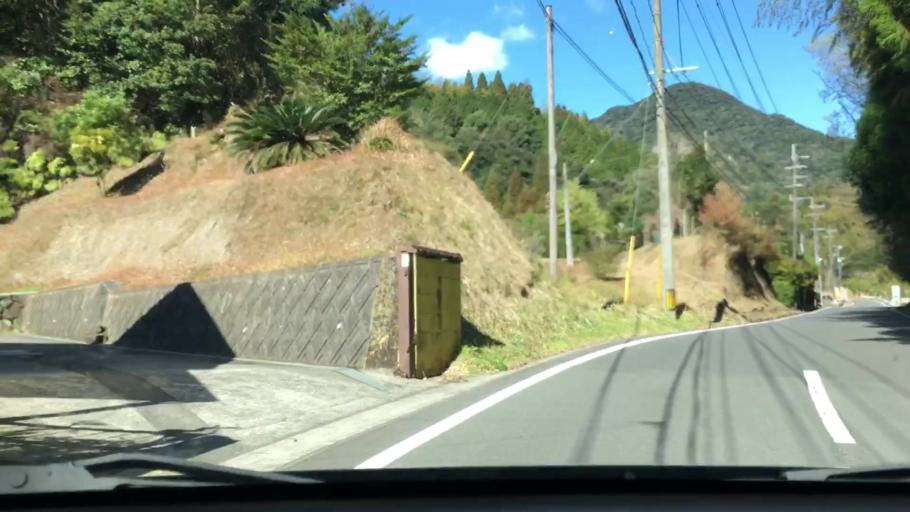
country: JP
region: Kagoshima
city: Ijuin
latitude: 31.7111
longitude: 130.4383
